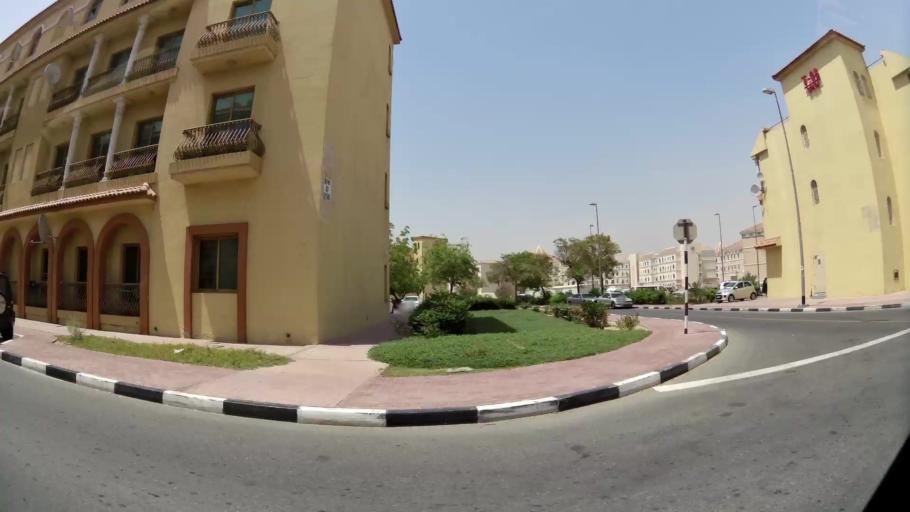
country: AE
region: Ash Shariqah
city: Sharjah
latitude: 25.1653
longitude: 55.3989
